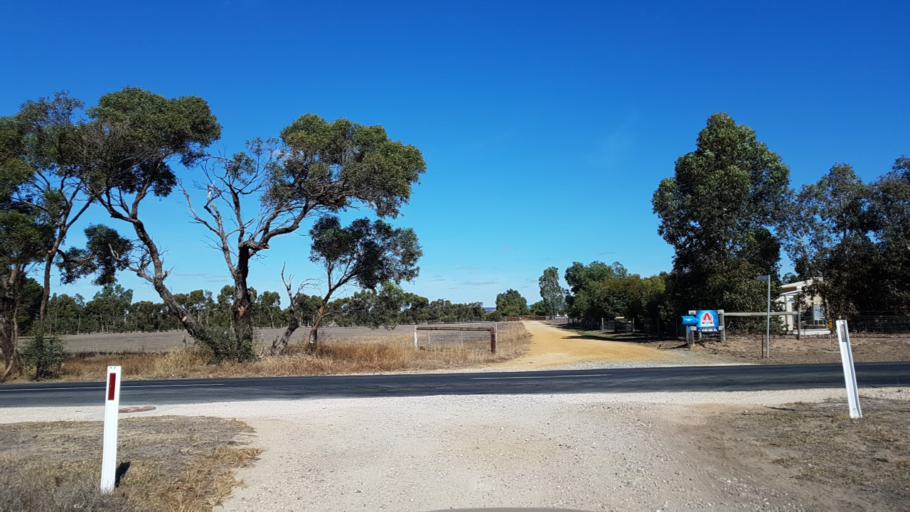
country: AU
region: South Australia
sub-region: Alexandrina
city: Goolwa
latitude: -35.3813
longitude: 138.8239
